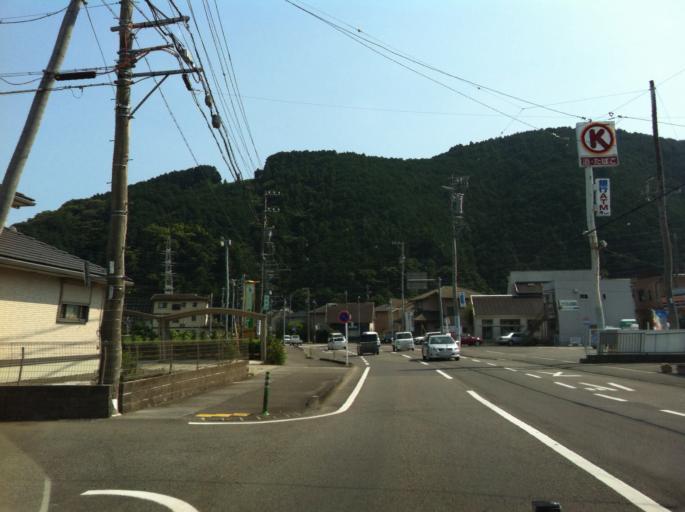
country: JP
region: Shizuoka
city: Shizuoka-shi
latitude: 35.0437
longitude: 138.3657
